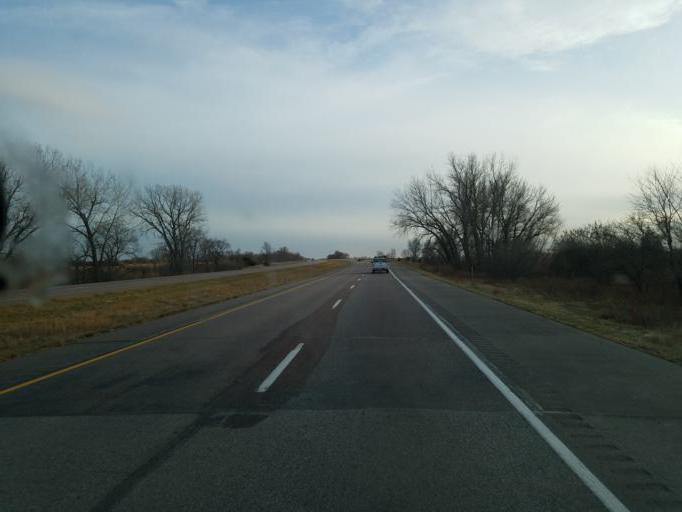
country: US
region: Nebraska
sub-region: Thurston County
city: Macy
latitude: 42.1574
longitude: -96.2236
